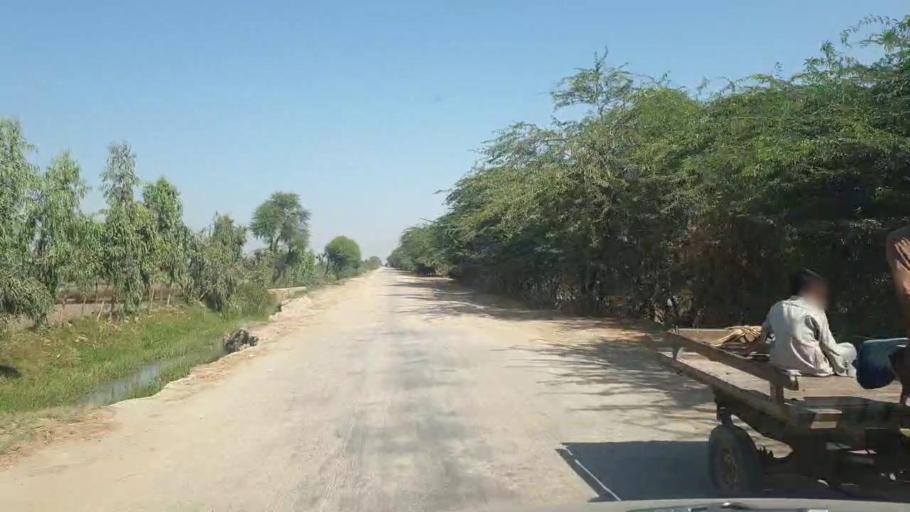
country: PK
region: Sindh
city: Tando Bago
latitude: 24.7968
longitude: 68.9758
